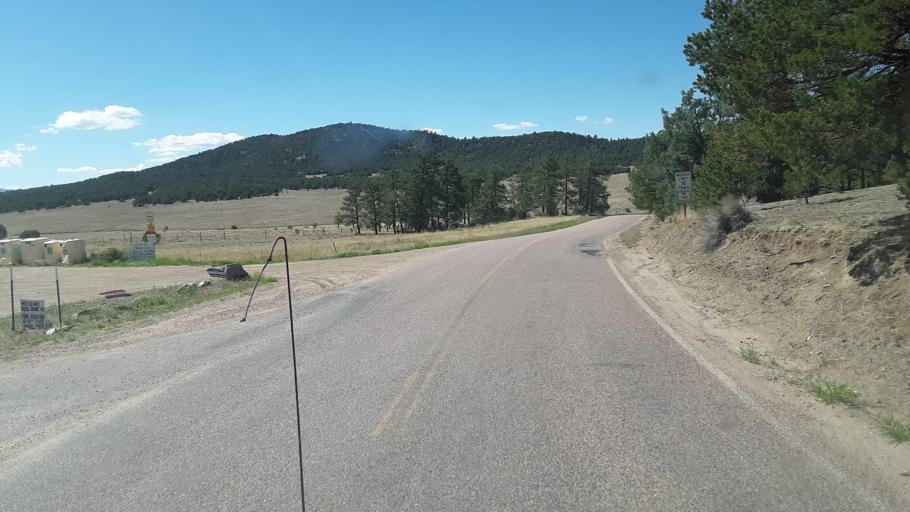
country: US
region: Colorado
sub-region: Custer County
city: Westcliffe
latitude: 38.3498
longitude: -105.4814
